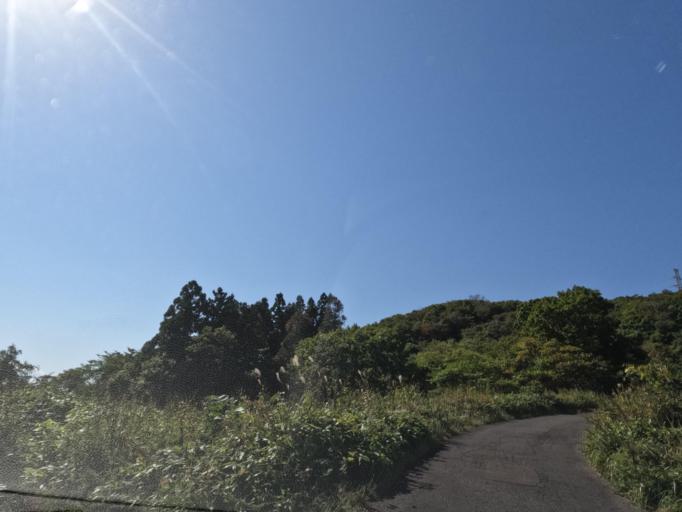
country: JP
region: Hokkaido
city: Muroran
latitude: 42.3671
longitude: 141.0239
